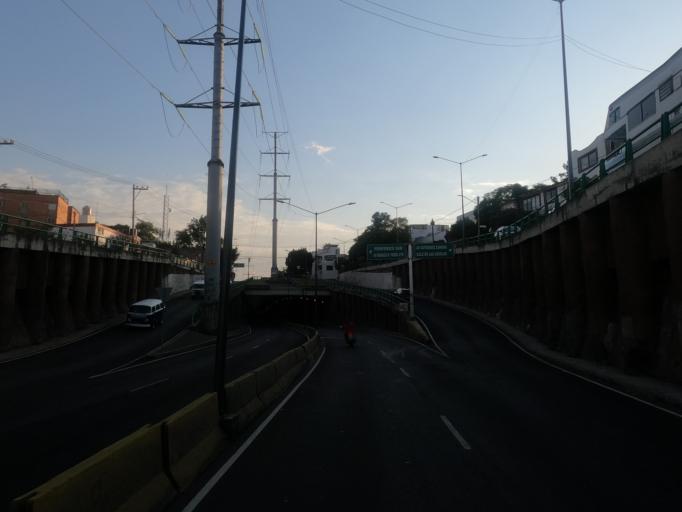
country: MX
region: Mexico City
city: Alvaro Obregon
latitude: 19.3606
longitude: -99.2064
